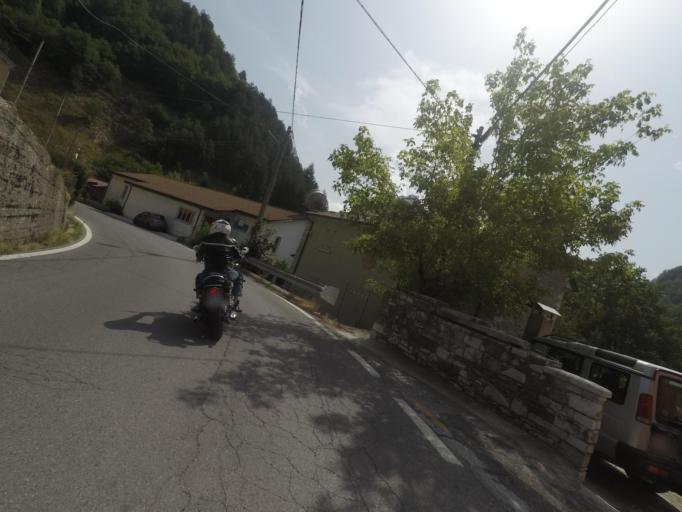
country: IT
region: Tuscany
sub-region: Provincia di Lucca
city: Fontana delle Monache
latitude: 44.0604
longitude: 10.2553
